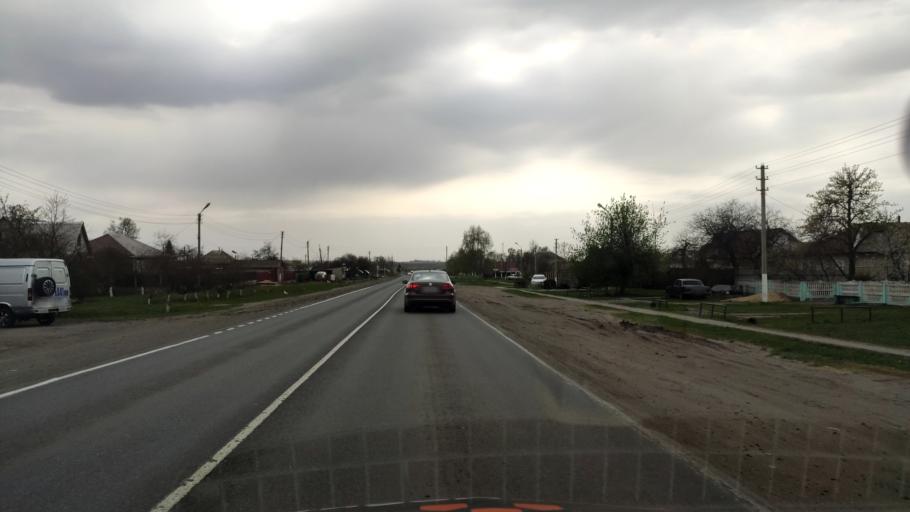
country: RU
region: Kursk
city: Gorshechnoye
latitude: 51.5218
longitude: 38.0206
